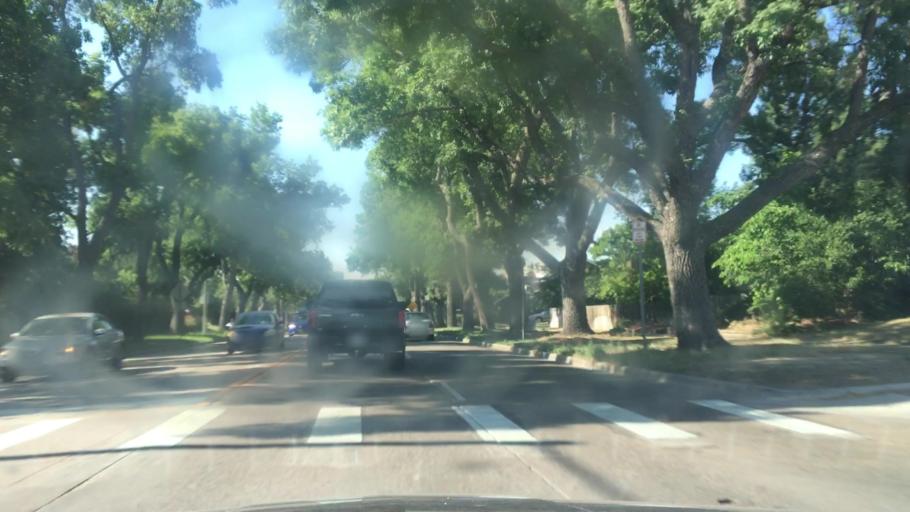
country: US
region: Colorado
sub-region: Arapahoe County
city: Glendale
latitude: 39.6893
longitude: -104.9594
